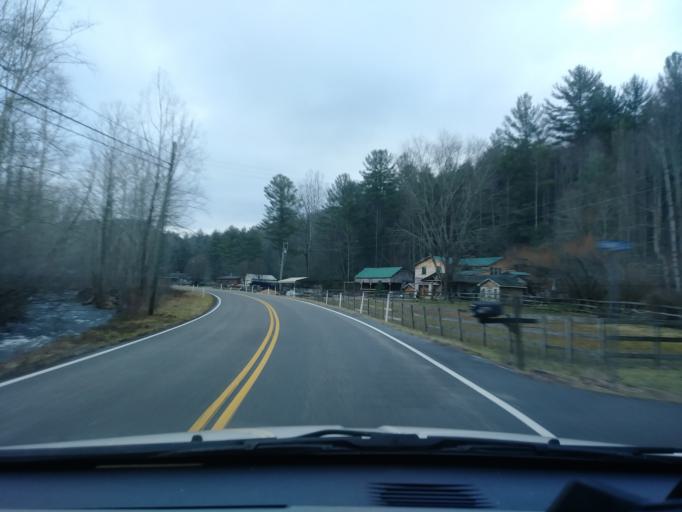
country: US
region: Tennessee
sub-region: Unicoi County
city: Unicoi
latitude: 36.1759
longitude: -82.2906
